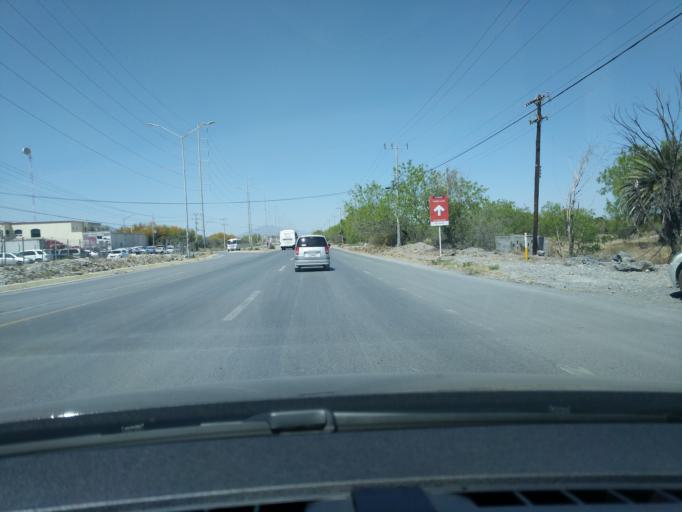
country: MX
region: Nuevo Leon
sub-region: Salinas Victoria
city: Emiliano Zapata
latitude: 25.9048
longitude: -100.2644
